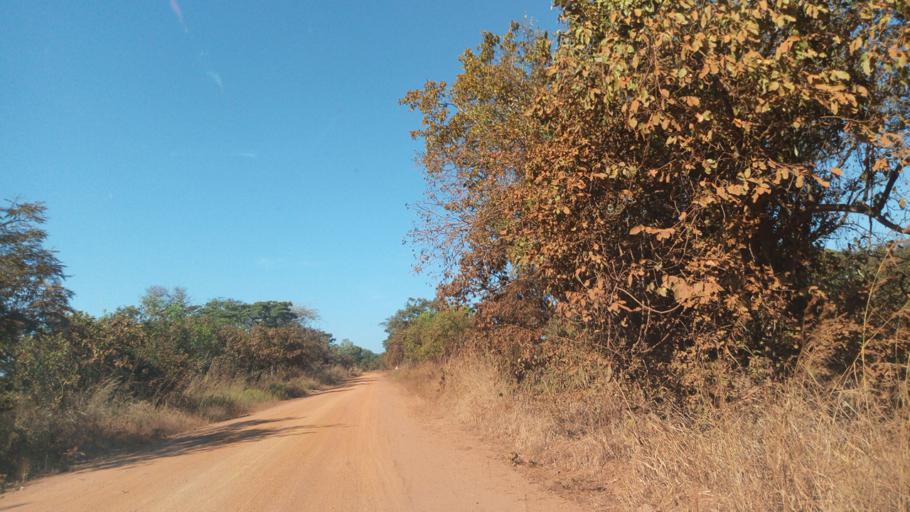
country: ZM
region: Luapula
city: Mwense
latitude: -10.6560
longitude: 28.4080
